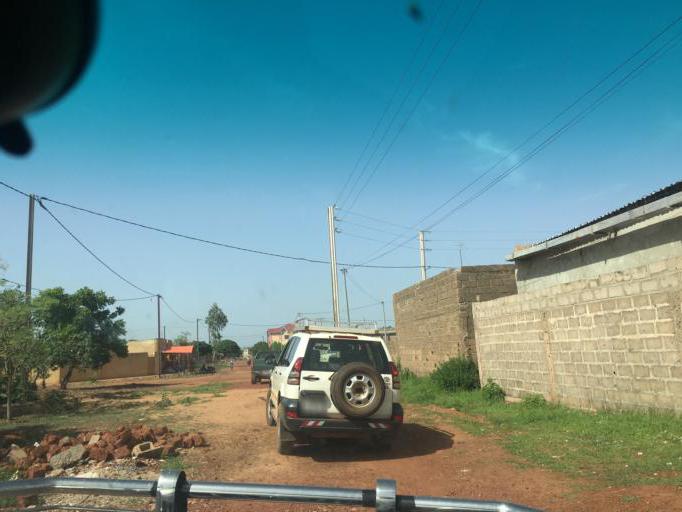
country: BF
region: High-Basins
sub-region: Province du Houet
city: Bobo-Dioulasso
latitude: 11.1641
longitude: -4.2380
